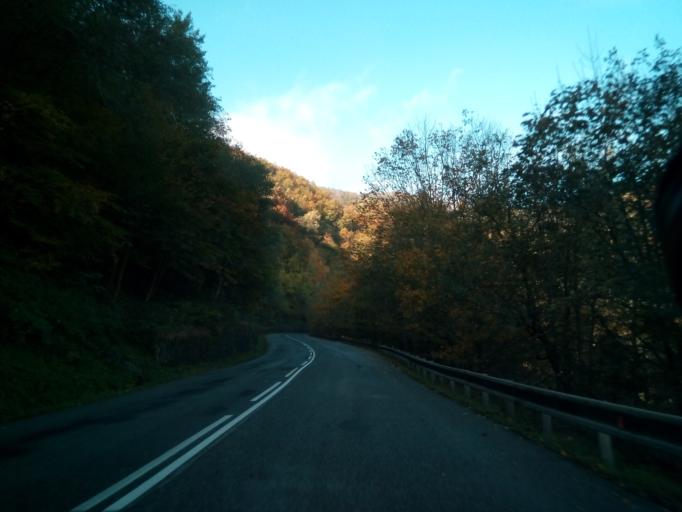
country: SK
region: Kosicky
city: Gelnica
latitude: 48.8888
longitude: 21.0031
